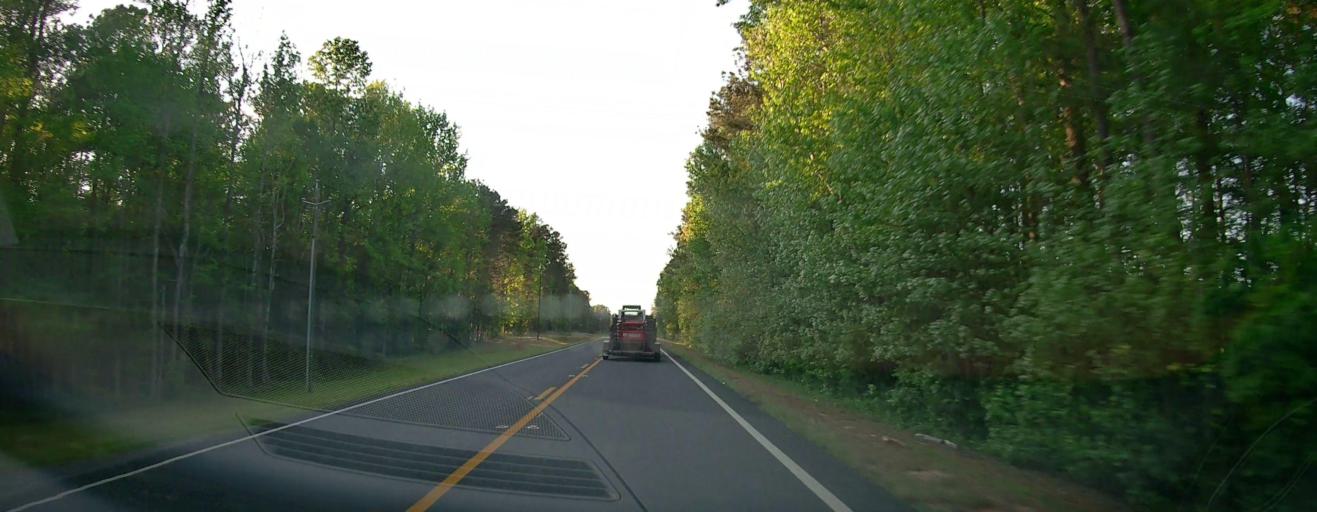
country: US
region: Georgia
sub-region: Jasper County
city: Monticello
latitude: 33.4844
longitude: -83.6472
